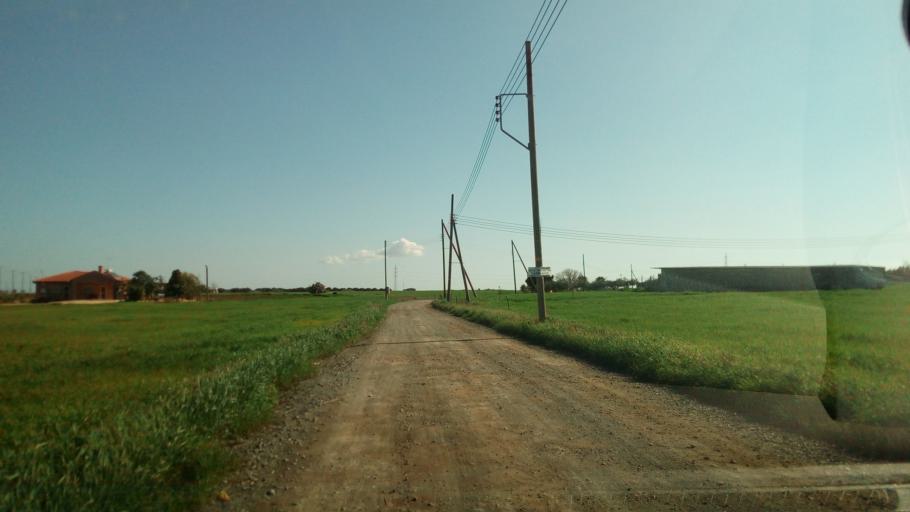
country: CY
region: Ammochostos
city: Avgorou
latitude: 35.0405
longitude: 33.8551
